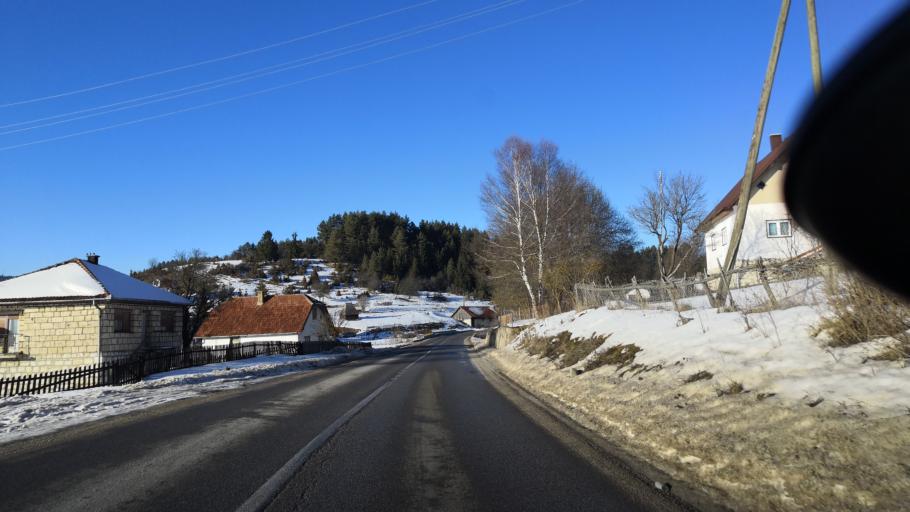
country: BA
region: Republika Srpska
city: Sokolac
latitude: 44.0009
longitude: 18.8811
